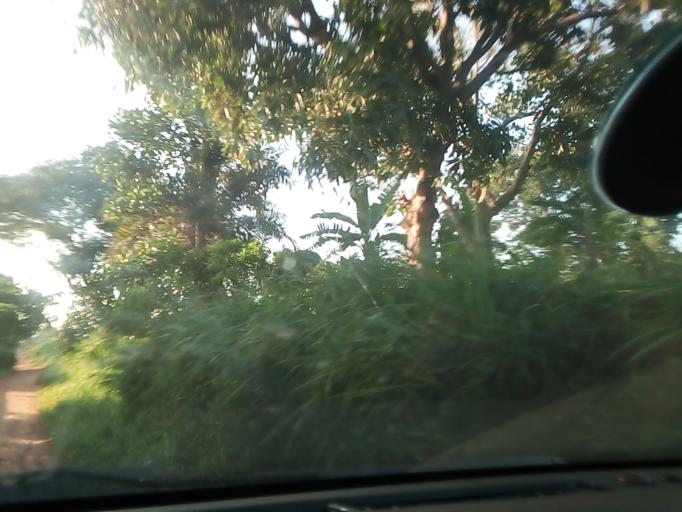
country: UG
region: Central Region
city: Masaka
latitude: -0.3333
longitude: 31.7559
